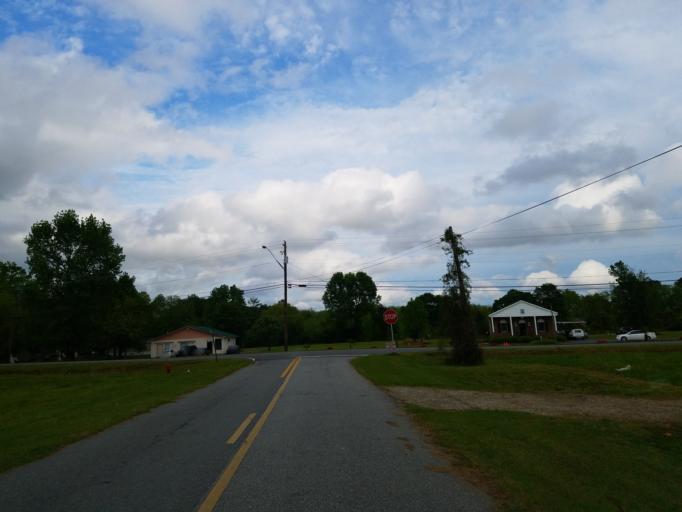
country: US
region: Georgia
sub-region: Dooly County
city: Unadilla
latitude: 32.2533
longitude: -83.7405
